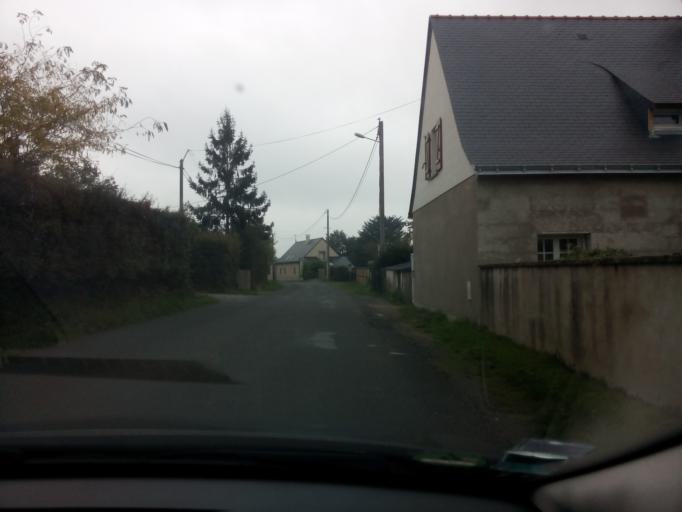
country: FR
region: Pays de la Loire
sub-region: Departement de Maine-et-Loire
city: Soulaire-et-Bourg
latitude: 47.5922
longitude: -0.5550
